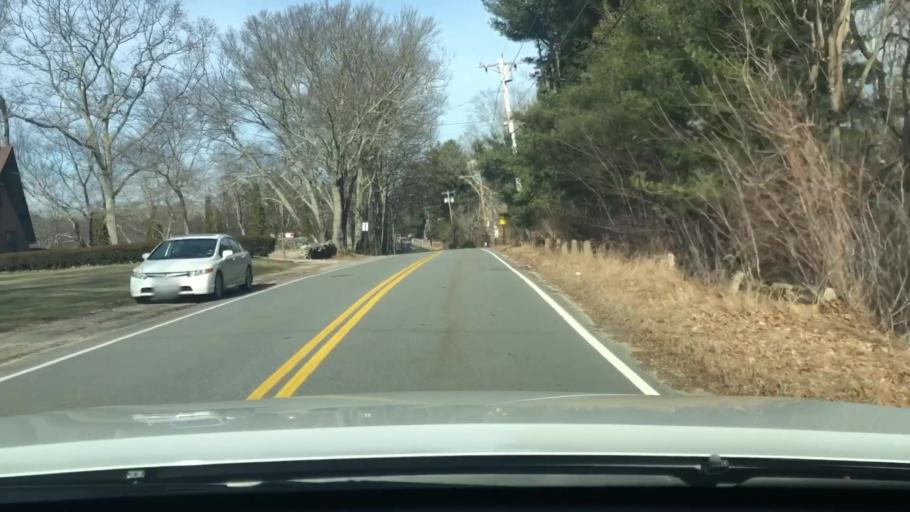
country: US
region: Massachusetts
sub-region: Worcester County
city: Blackstone
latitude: 42.0474
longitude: -71.5202
